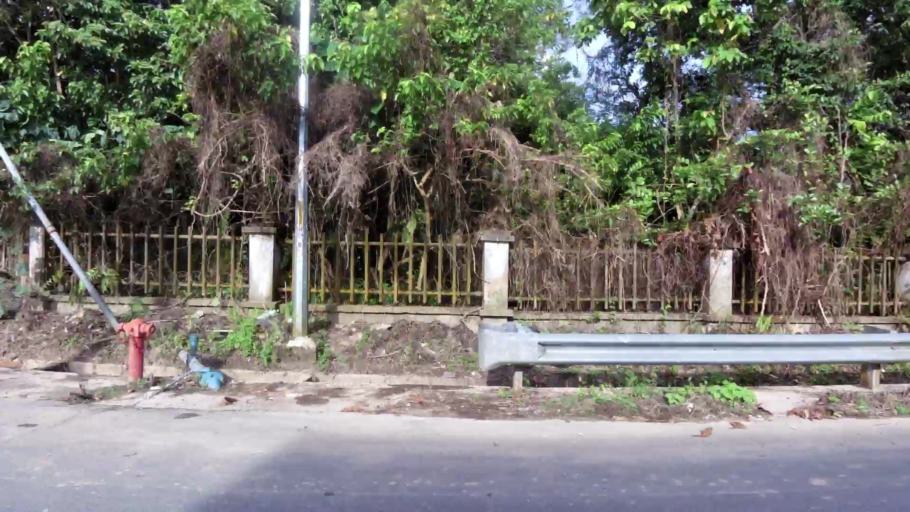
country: BN
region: Brunei and Muara
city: Bandar Seri Begawan
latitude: 4.9083
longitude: 114.8970
